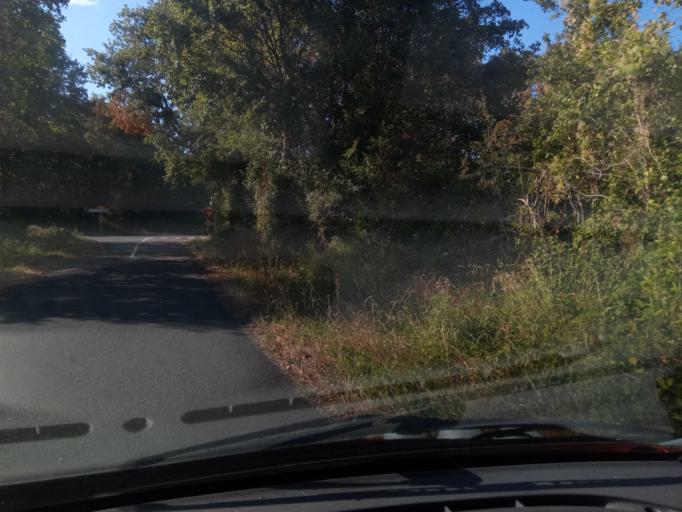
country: FR
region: Poitou-Charentes
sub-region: Departement de la Vienne
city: Montmorillon
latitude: 46.4914
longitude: 0.8004
